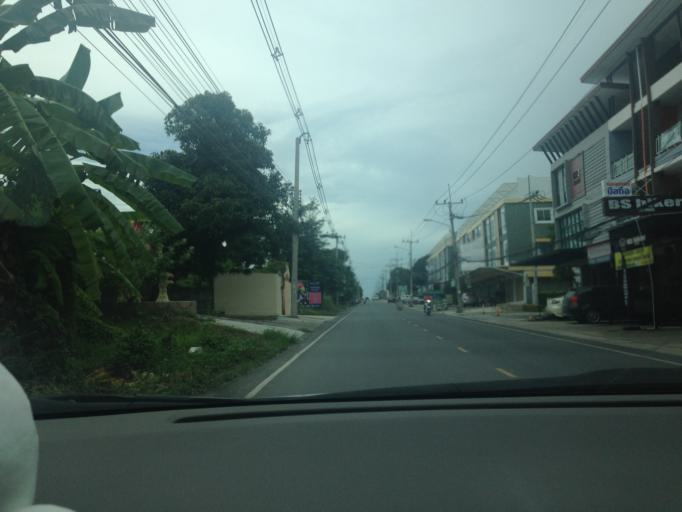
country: TH
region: Chon Buri
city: Chon Buri
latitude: 13.3263
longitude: 100.9272
